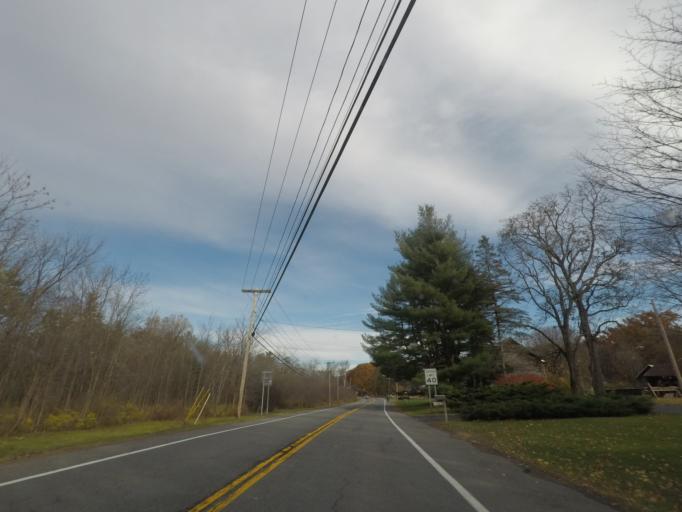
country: US
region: New York
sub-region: Albany County
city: Voorheesville
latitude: 42.6458
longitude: -73.9501
